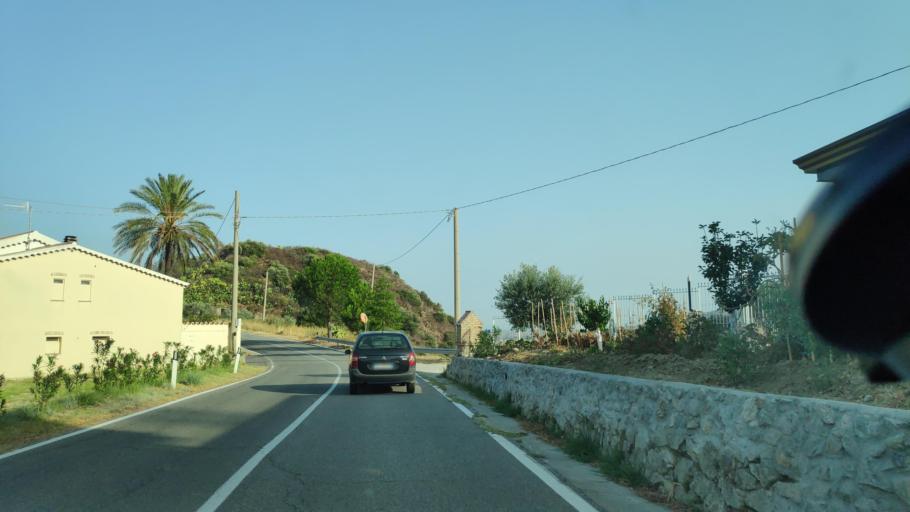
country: IT
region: Calabria
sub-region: Provincia di Catanzaro
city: Sant'Andrea Ionio Marina
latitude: 38.6211
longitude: 16.5405
